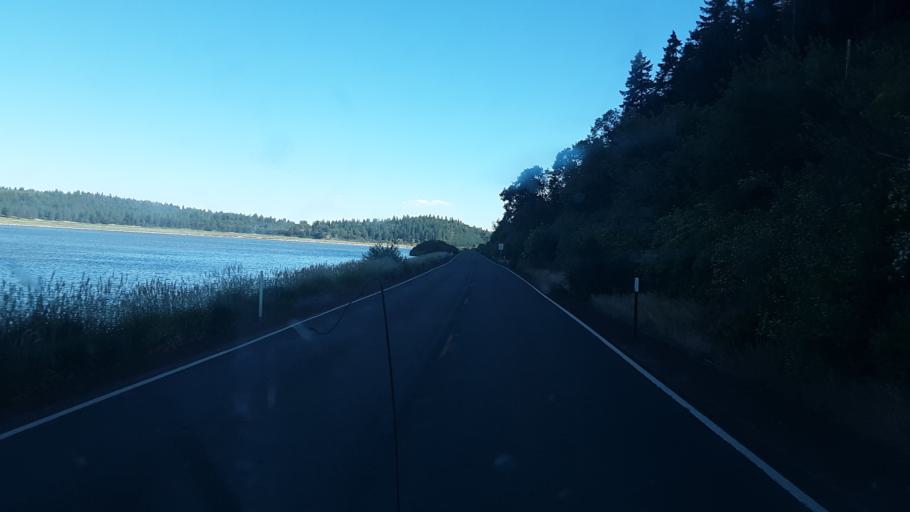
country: US
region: Oregon
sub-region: Klamath County
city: Klamath Falls
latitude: 42.2991
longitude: -121.9333
